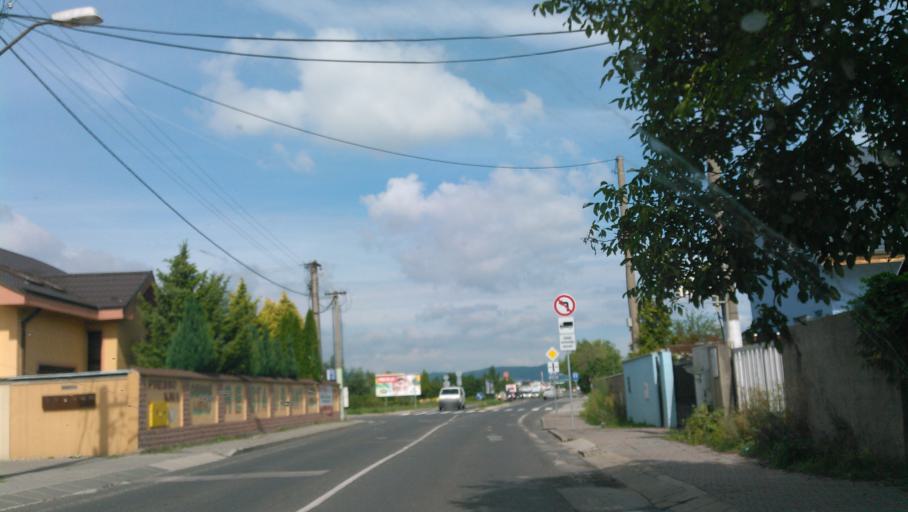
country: SK
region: Bratislavsky
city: Bratislava
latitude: 48.1540
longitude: 17.1958
